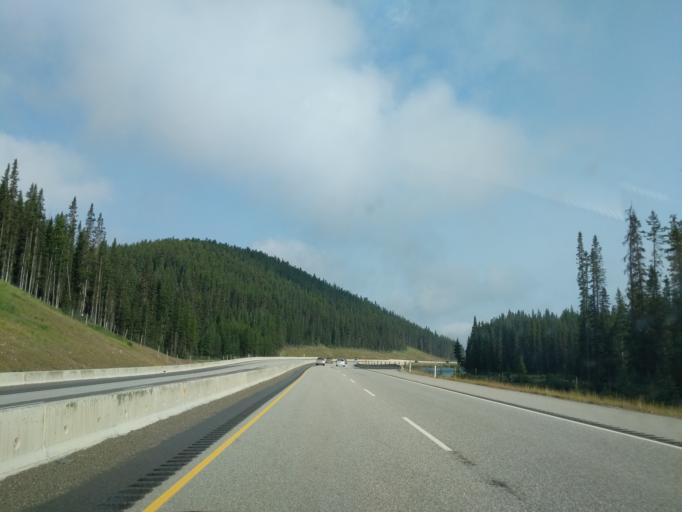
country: CA
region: Alberta
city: Lake Louise
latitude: 51.3271
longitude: -116.0495
